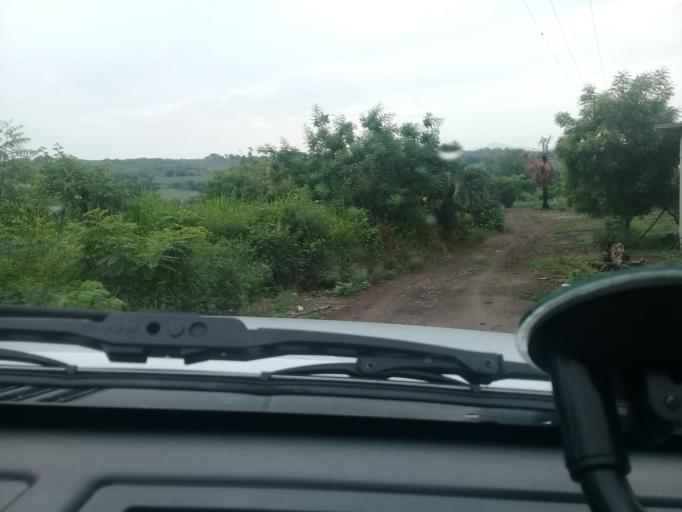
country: MX
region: Veracruz
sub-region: Puente Nacional
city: Chichicaxtle
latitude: 19.3689
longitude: -96.4342
